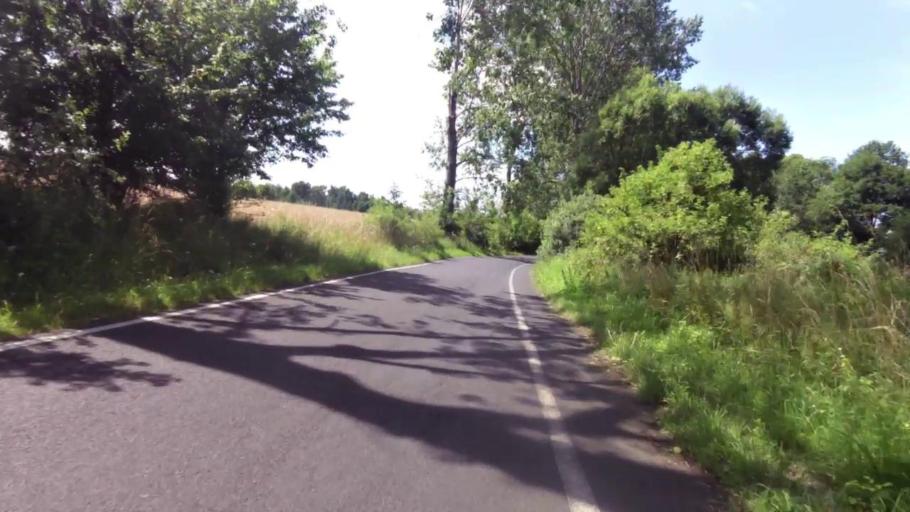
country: PL
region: West Pomeranian Voivodeship
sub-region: Powiat stargardzki
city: Insko
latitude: 53.4313
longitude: 15.5208
